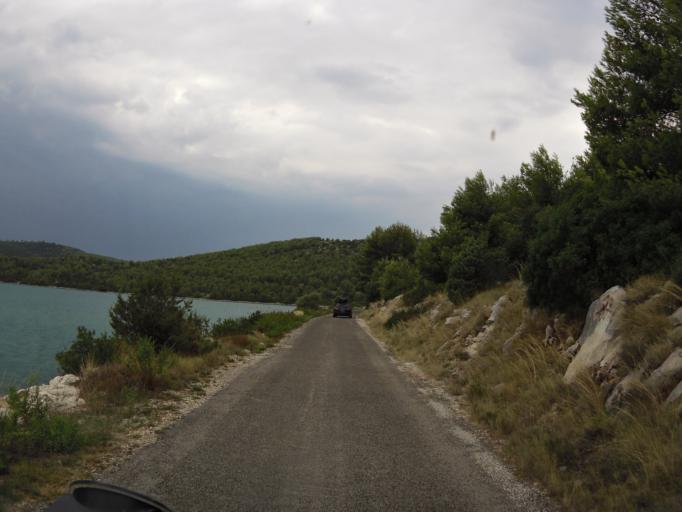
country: HR
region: Zadarska
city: Sali
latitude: 43.9229
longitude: 15.1319
